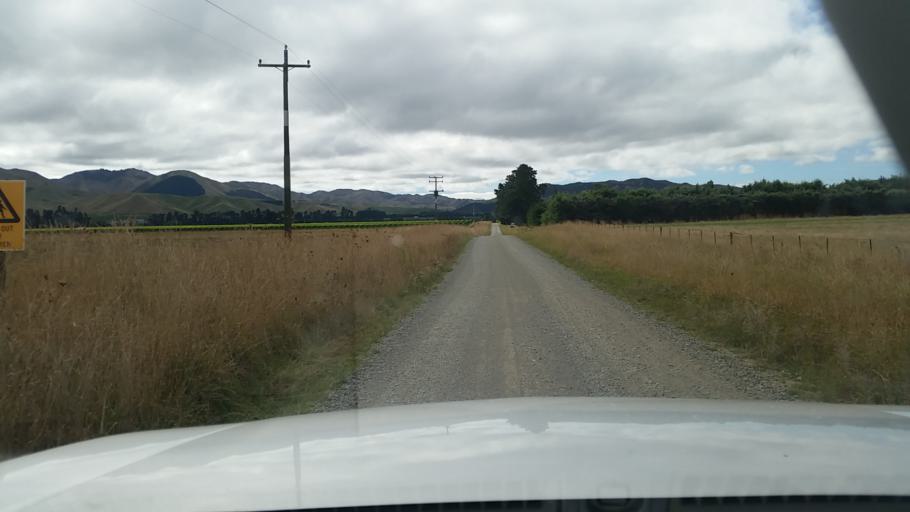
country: NZ
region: Marlborough
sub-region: Marlborough District
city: Blenheim
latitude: -41.6787
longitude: 174.0387
